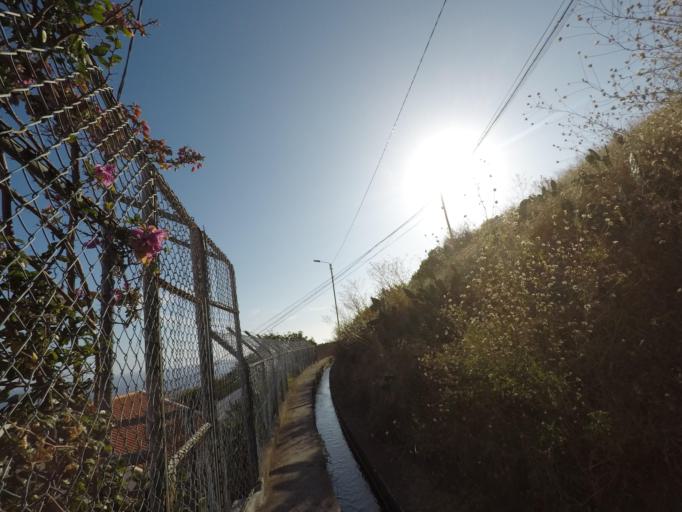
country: PT
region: Madeira
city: Camara de Lobos
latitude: 32.6398
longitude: -16.9387
